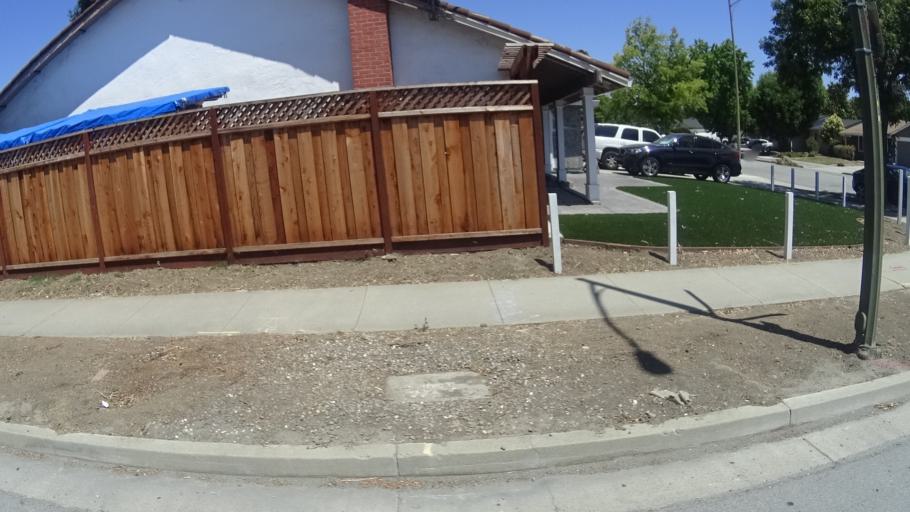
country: US
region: California
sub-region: Santa Clara County
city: Seven Trees
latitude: 37.2625
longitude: -121.8309
